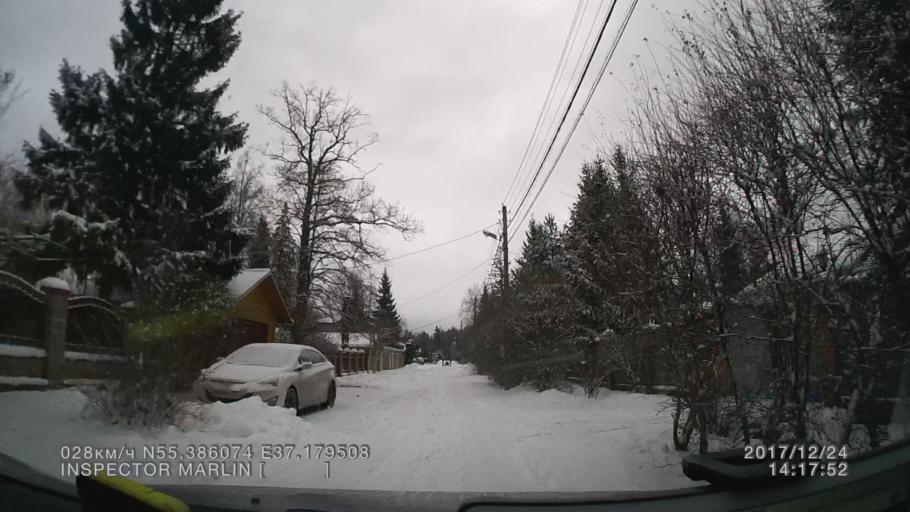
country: RU
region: Moskovskaya
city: Troitsk
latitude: 55.3861
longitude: 37.1795
